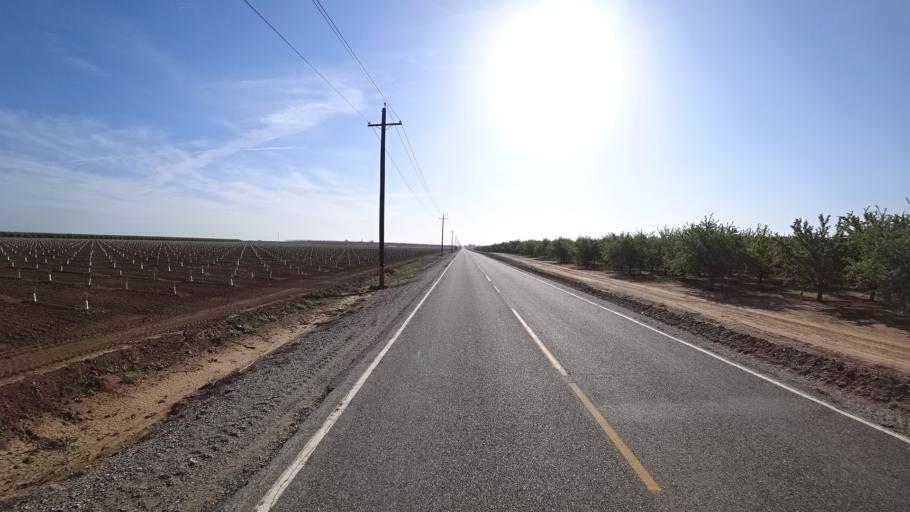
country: US
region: California
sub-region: Glenn County
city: Willows
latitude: 39.5388
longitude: -122.2385
